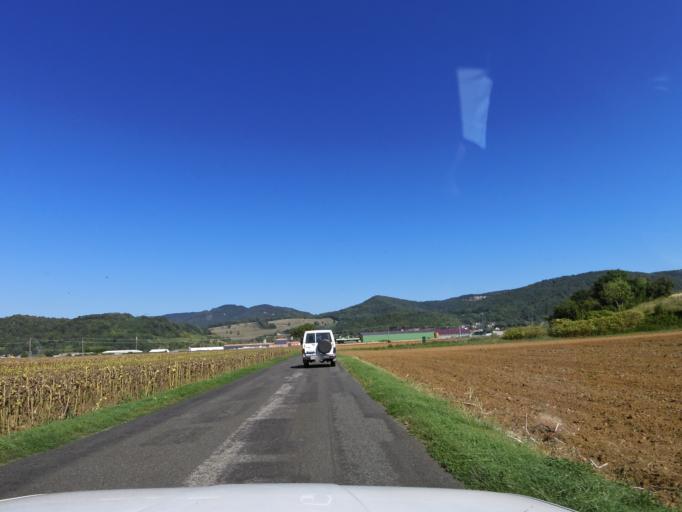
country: FR
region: Rhone-Alpes
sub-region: Departement de l'Ain
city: Vaux-en-Bugey
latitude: 45.9244
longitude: 5.3302
